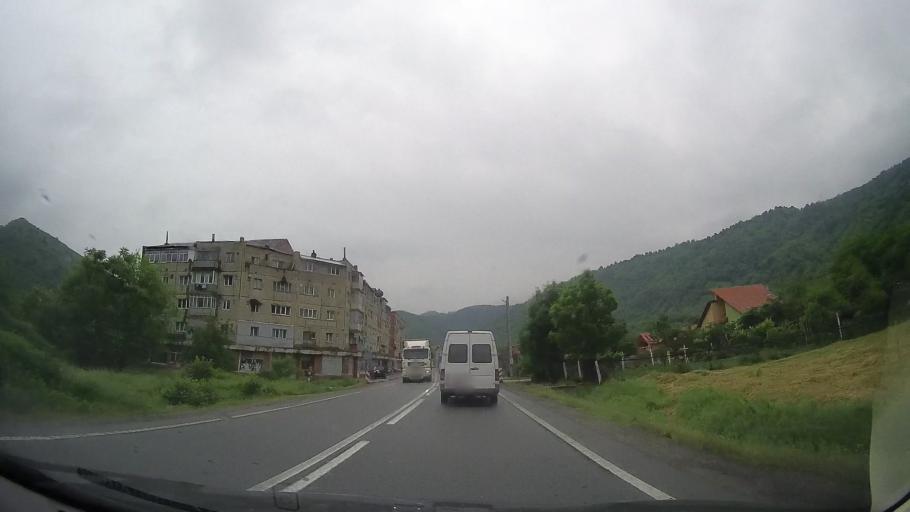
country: RO
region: Caras-Severin
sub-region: Comuna Toplet
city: Toplet
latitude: 44.8137
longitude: 22.3860
